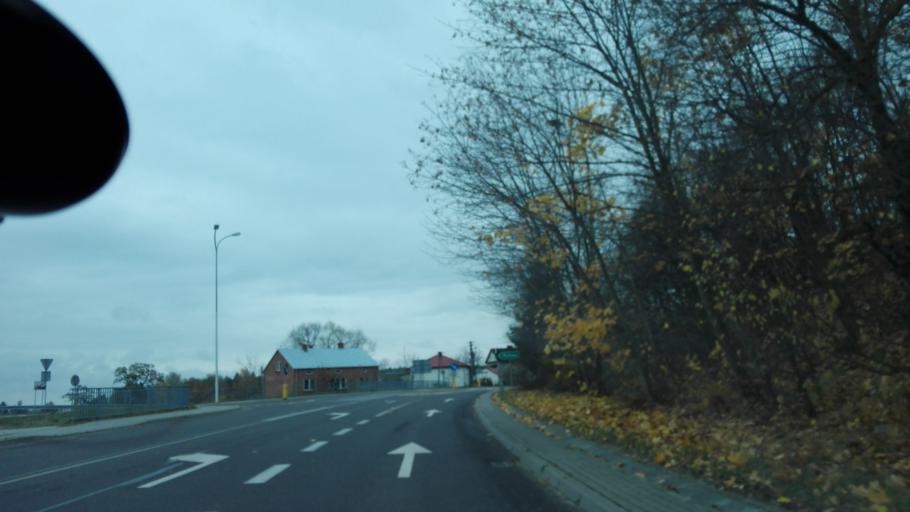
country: PL
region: Lublin Voivodeship
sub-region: Powiat pulawski
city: Pulawy
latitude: 51.4365
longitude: 21.9122
